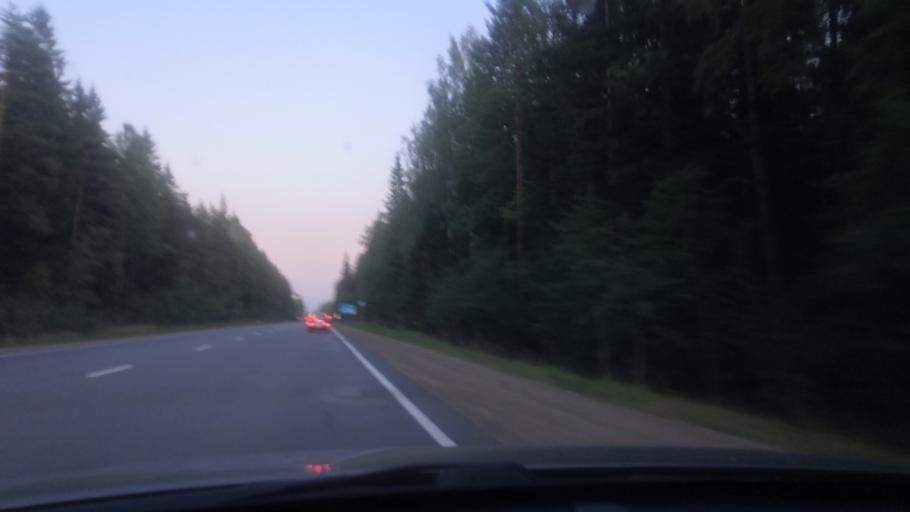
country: RU
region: St.-Petersburg
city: Pesochnyy
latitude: 60.1841
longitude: 30.1207
